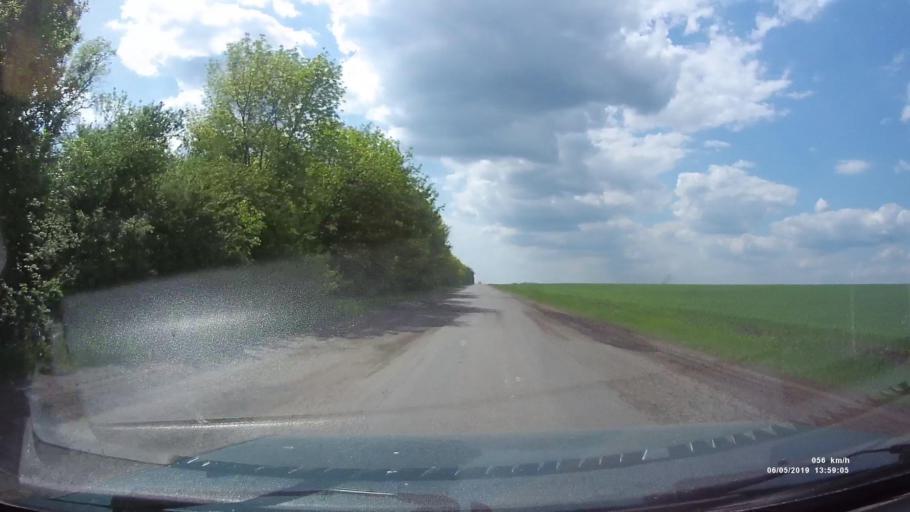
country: RU
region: Rostov
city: Shakhty
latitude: 47.6854
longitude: 40.4040
